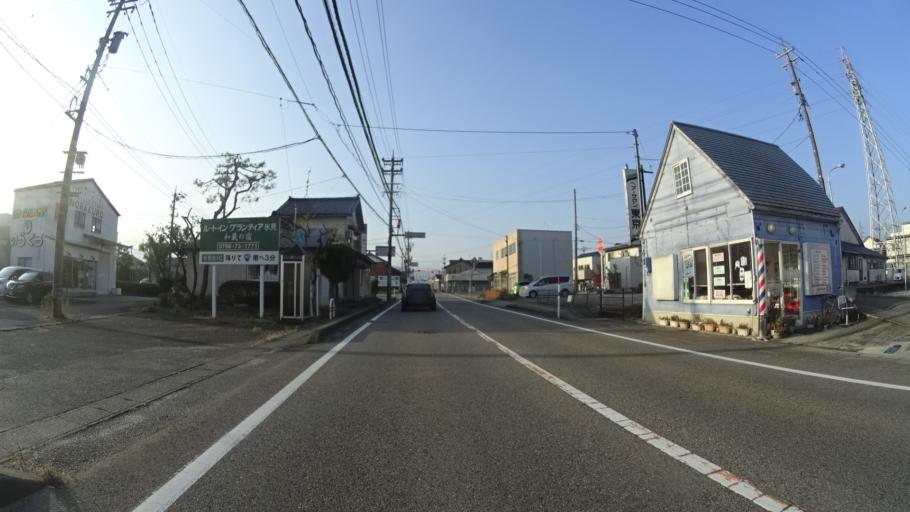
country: JP
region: Ishikawa
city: Nanao
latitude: 37.0343
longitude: 136.9684
